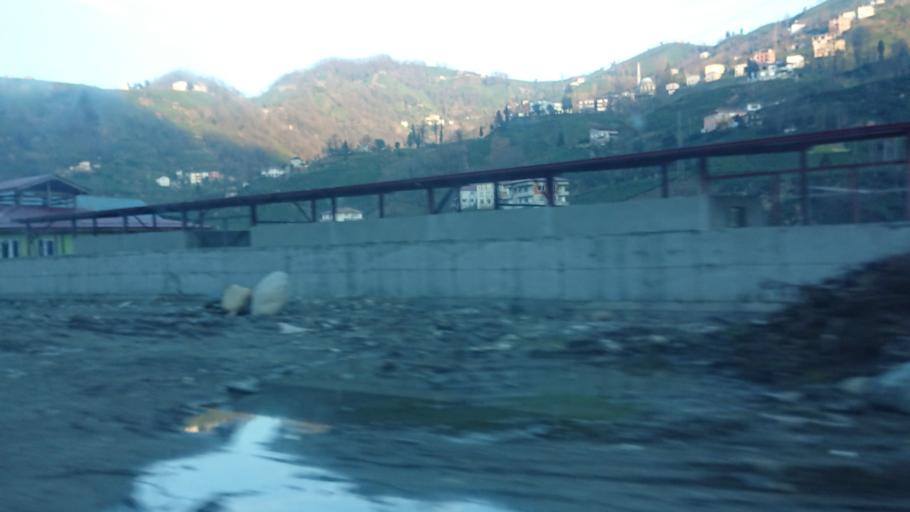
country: TR
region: Rize
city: Gundogdu
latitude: 41.0246
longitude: 40.5772
